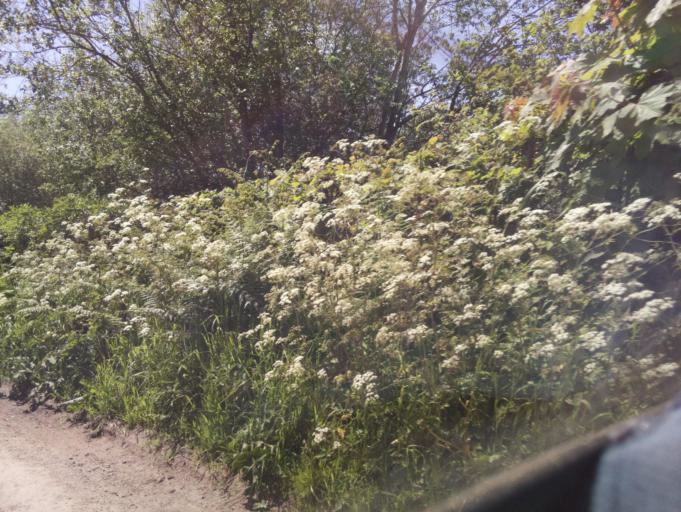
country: GB
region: Wales
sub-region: Monmouthshire
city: Llangwm
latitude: 51.6736
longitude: -2.7707
